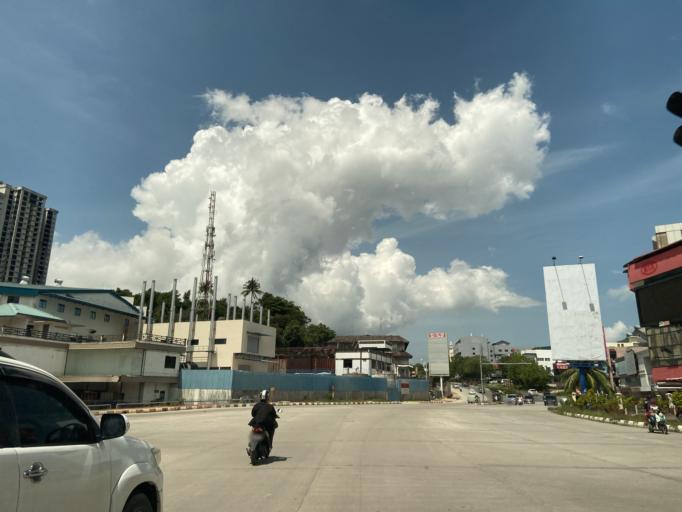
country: SG
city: Singapore
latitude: 1.1410
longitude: 104.0158
